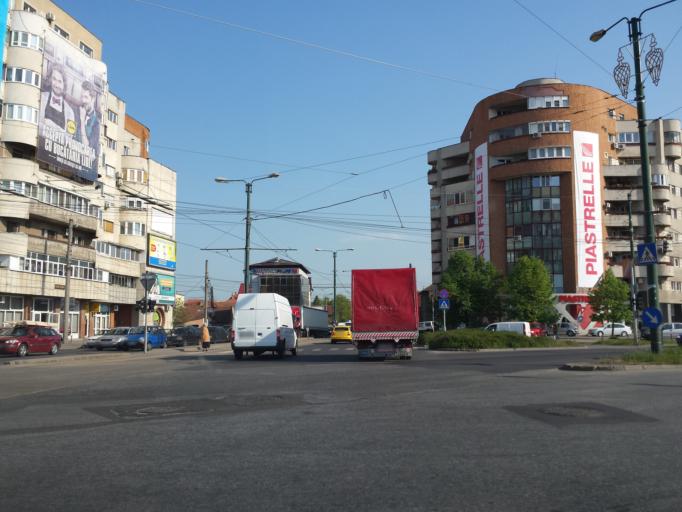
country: RO
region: Timis
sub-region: Comuna Dumbravita
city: Dumbravita
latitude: 45.7655
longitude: 21.2607
